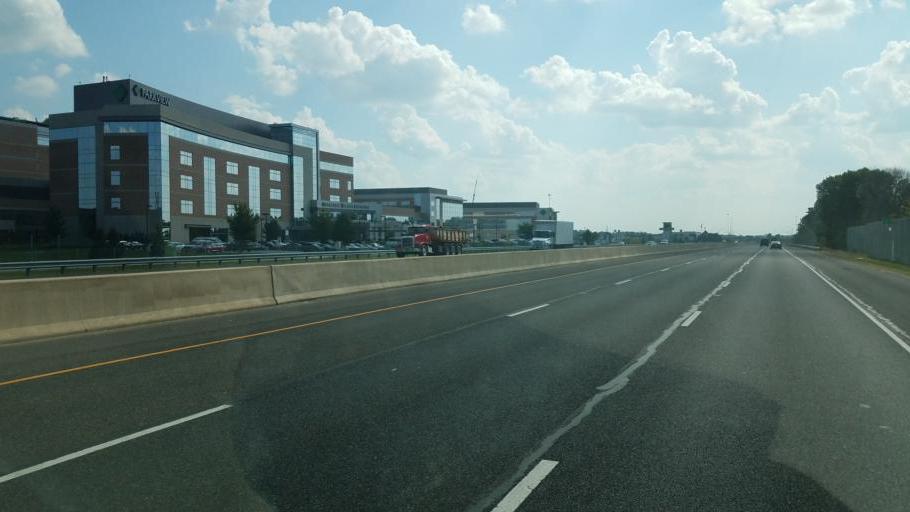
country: US
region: Indiana
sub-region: Allen County
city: Fort Wayne
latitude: 41.1884
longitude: -85.1040
